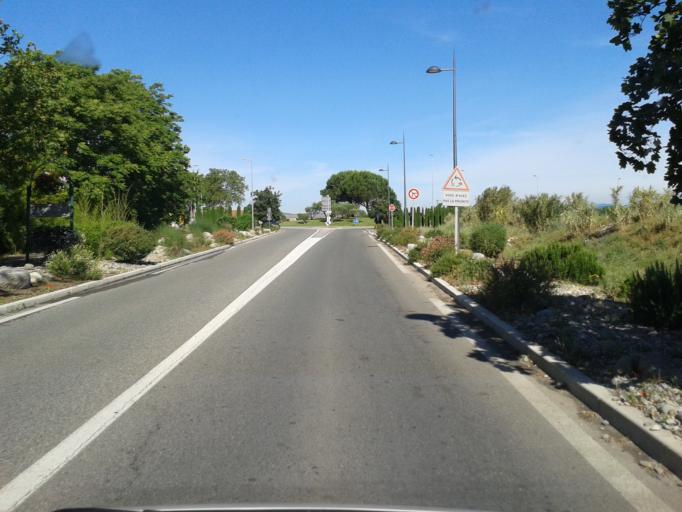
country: FR
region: Provence-Alpes-Cote d'Azur
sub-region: Departement des Bouches-du-Rhone
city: Peyrolles-en-Provence
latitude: 43.6459
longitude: 5.5751
